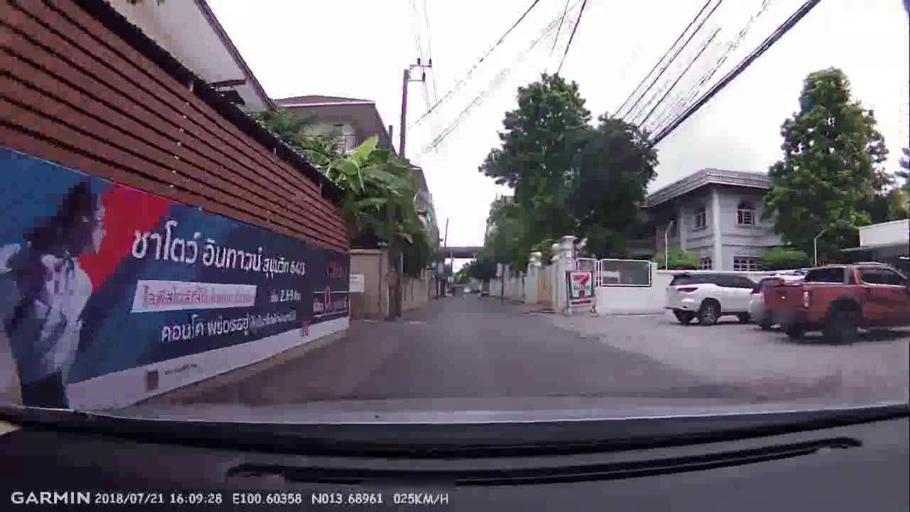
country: TH
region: Bangkok
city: Phra Khanong
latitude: 13.6896
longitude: 100.6035
